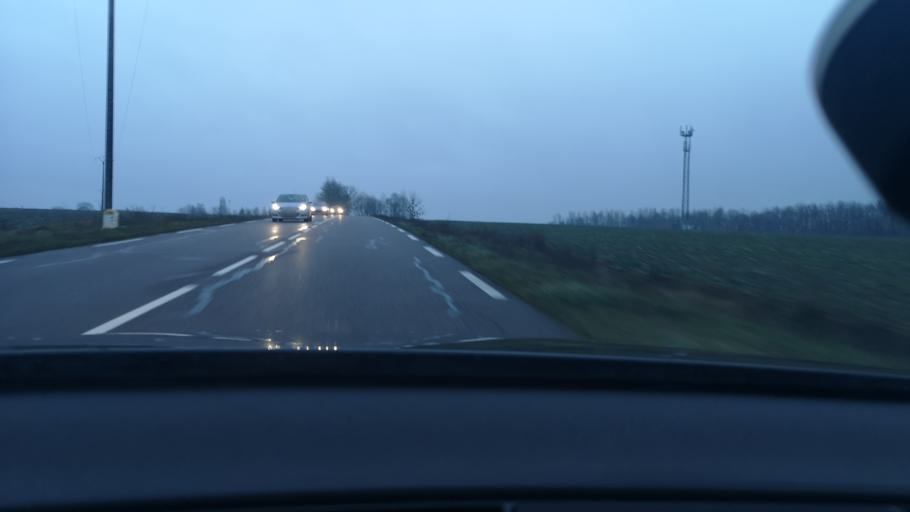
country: FR
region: Bourgogne
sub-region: Departement de la Cote-d'Or
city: Aiserey
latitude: 47.0912
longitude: 5.1056
